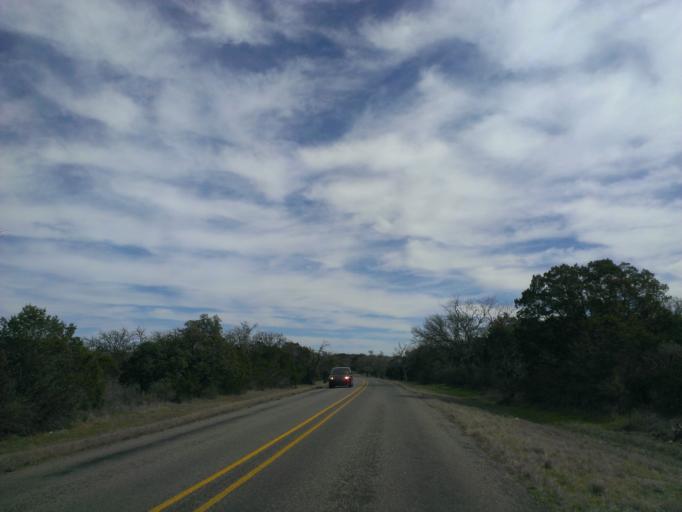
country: US
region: Texas
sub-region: Llano County
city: Buchanan Dam
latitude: 30.6963
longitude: -98.3702
